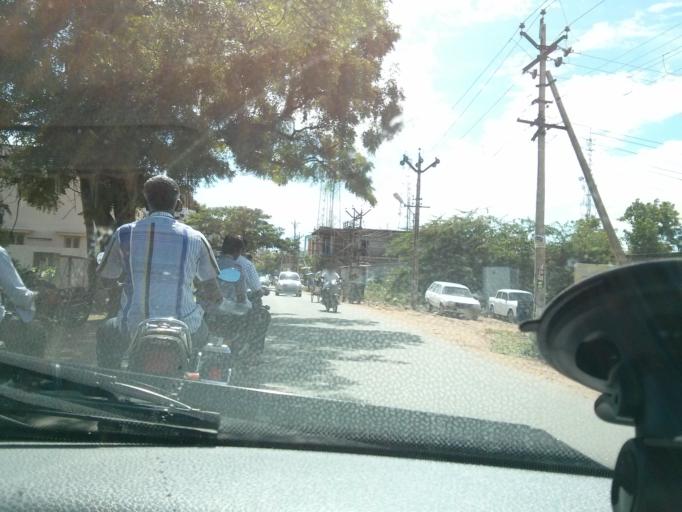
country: IN
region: Tamil Nadu
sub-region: Coimbatore
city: Coimbatore
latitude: 11.0395
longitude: 76.9308
